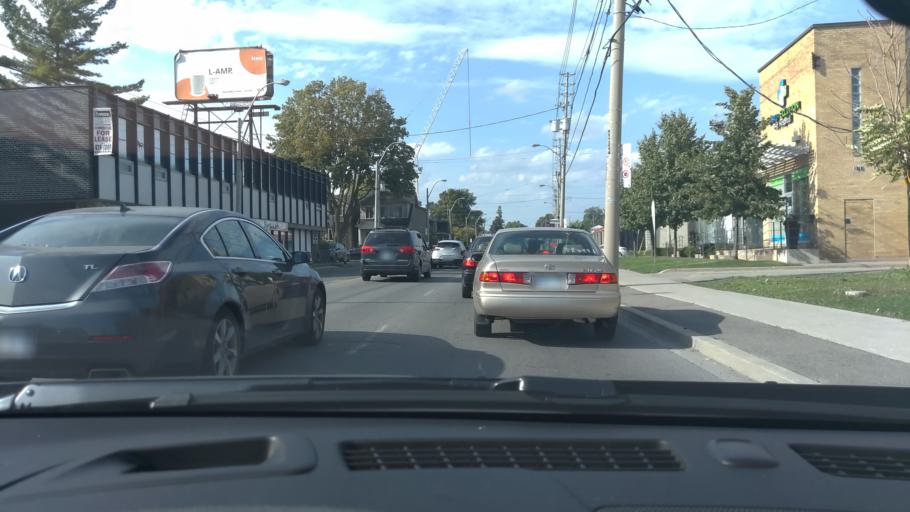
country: CA
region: Ontario
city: Toronto
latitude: 43.7111
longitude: -79.3638
